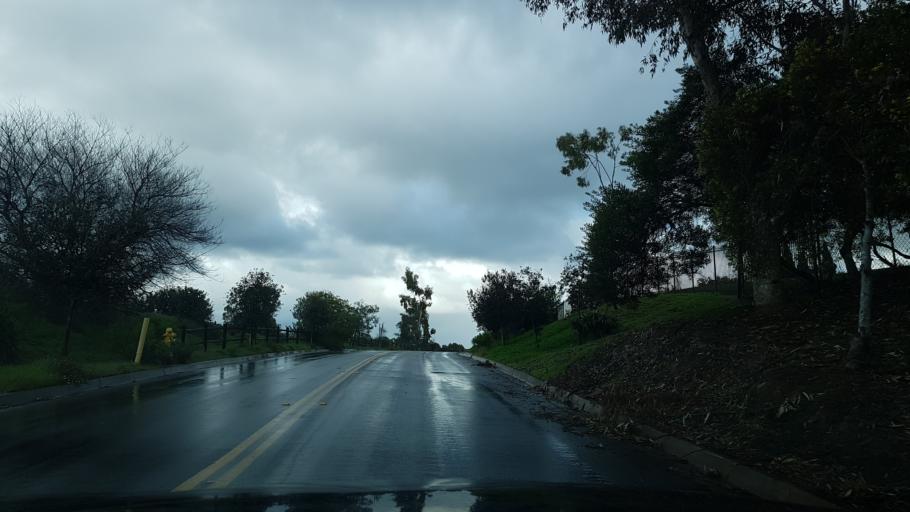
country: US
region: California
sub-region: San Diego County
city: Fairbanks Ranch
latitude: 32.9435
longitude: -117.1957
